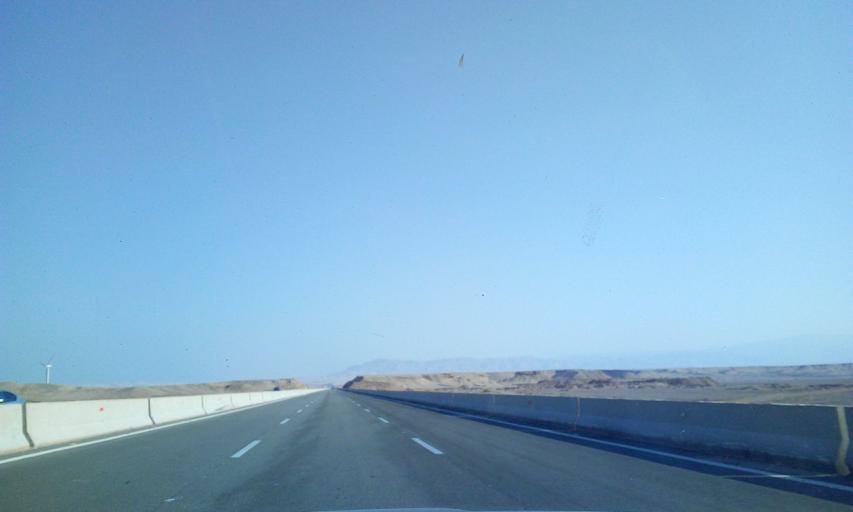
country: EG
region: As Suways
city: Ain Sukhna
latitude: 29.1683
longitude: 32.5080
